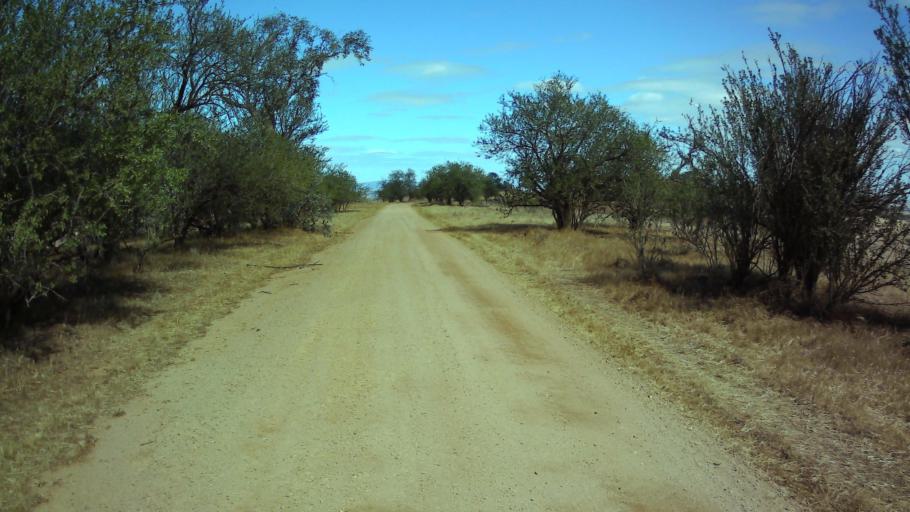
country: AU
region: New South Wales
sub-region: Young
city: Young
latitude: -34.1035
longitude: 148.3901
